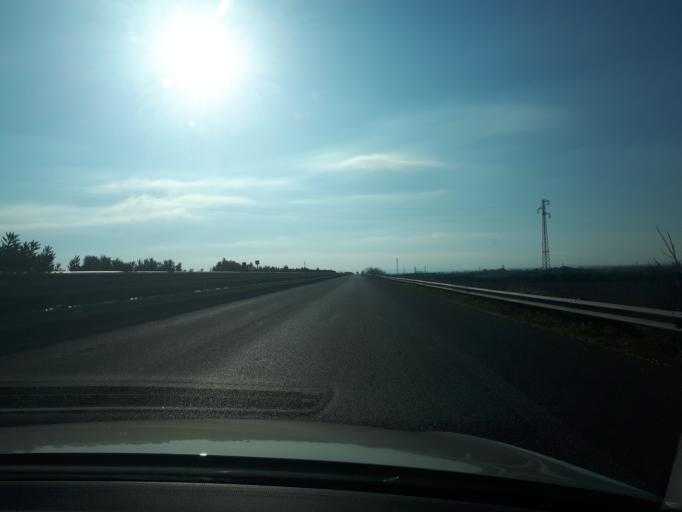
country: IT
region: Apulia
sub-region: Provincia di Foggia
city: Foggia
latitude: 41.4127
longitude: 15.5585
